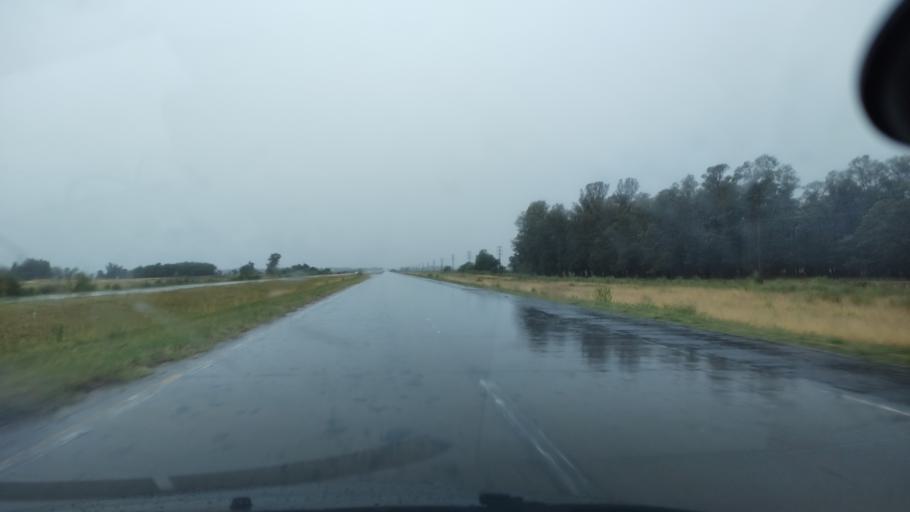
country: AR
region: Buenos Aires
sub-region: Partido de San Vicente
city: San Vicente
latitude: -35.0657
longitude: -58.4827
